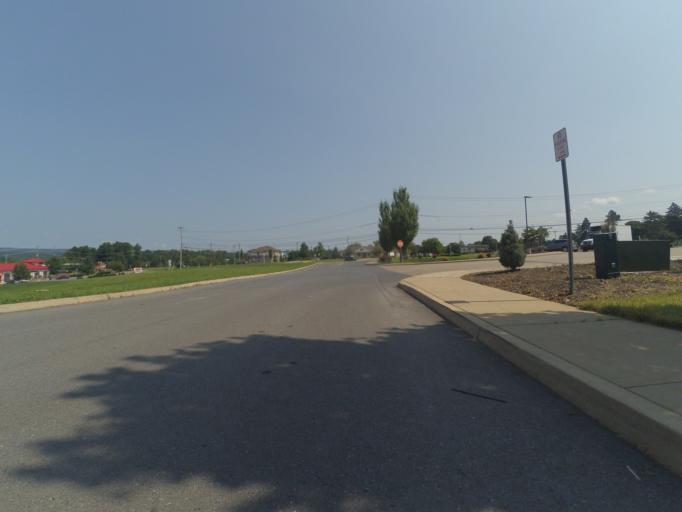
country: US
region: Pennsylvania
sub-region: Centre County
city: Houserville
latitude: 40.8363
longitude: -77.8027
